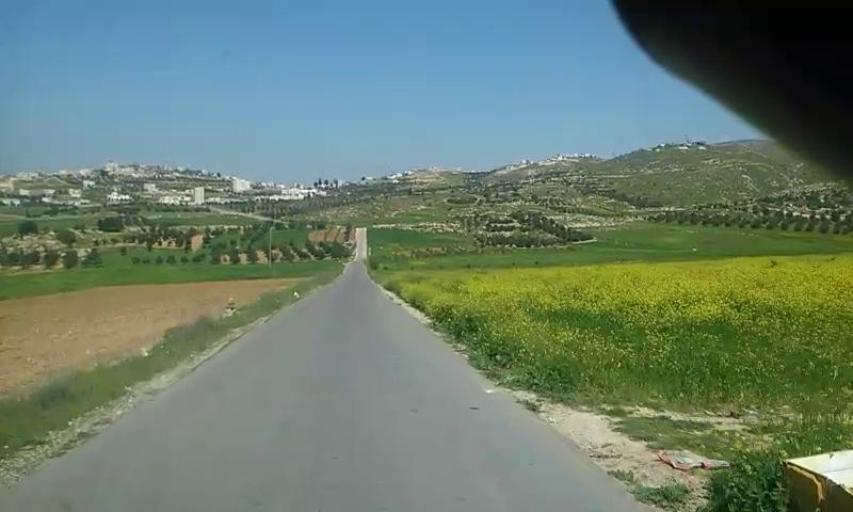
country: PS
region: West Bank
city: Al Majd
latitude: 31.4927
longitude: 34.9587
